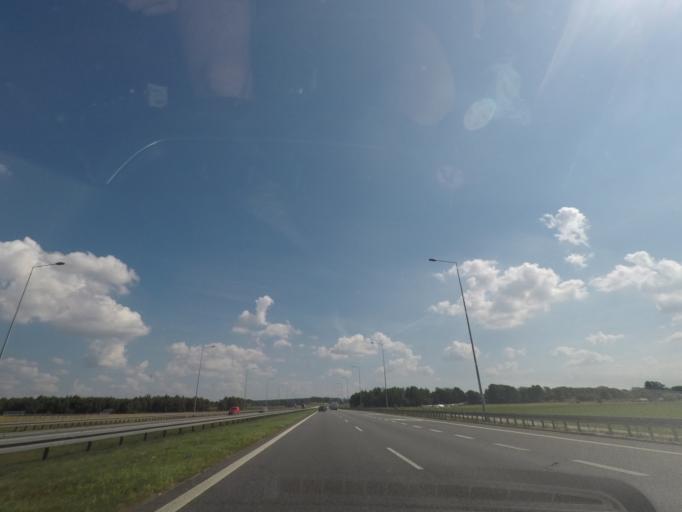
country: PL
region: Lodz Voivodeship
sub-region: Powiat zgierski
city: Strykow
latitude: 51.8782
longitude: 19.6471
